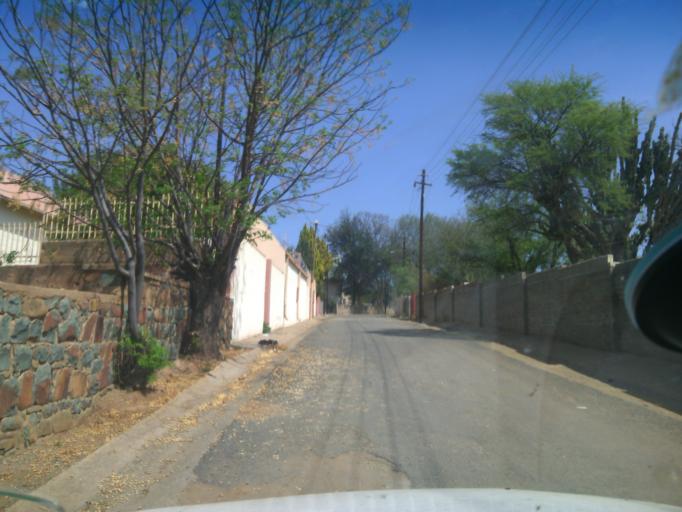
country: ZA
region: Northern Cape
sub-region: Frances Baard District Municipality
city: Barkly West
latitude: -28.5388
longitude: 24.5205
